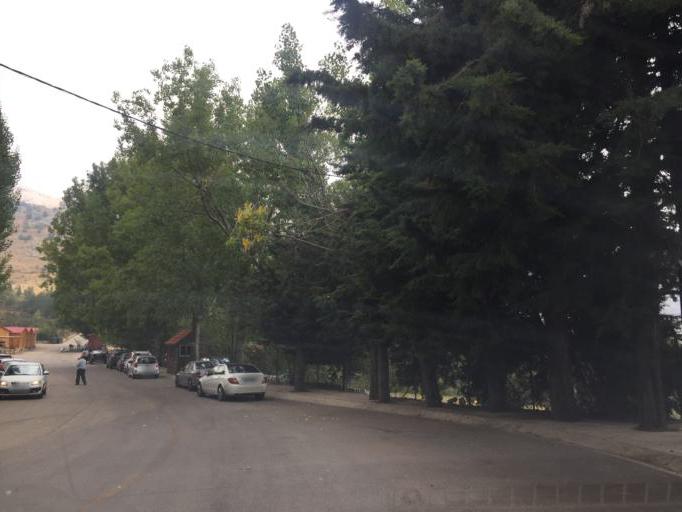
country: LB
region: Beqaa
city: Zahle
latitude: 33.9982
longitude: 35.8087
